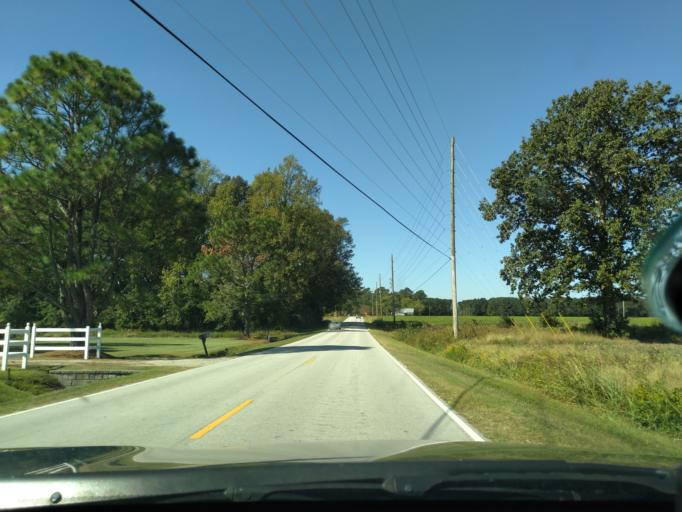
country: US
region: North Carolina
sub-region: Beaufort County
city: River Road
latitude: 35.5775
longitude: -76.9463
